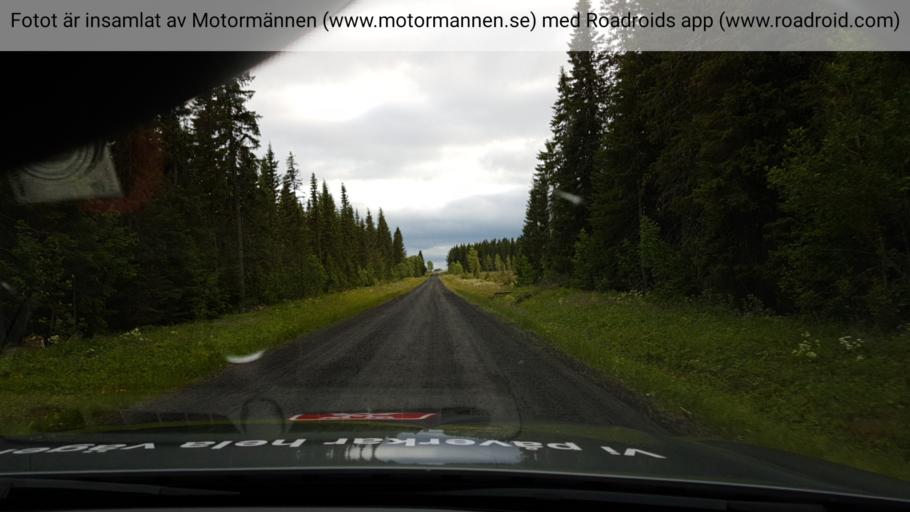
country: SE
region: Jaemtland
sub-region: OEstersunds Kommun
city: Lit
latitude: 63.6188
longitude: 15.0112
